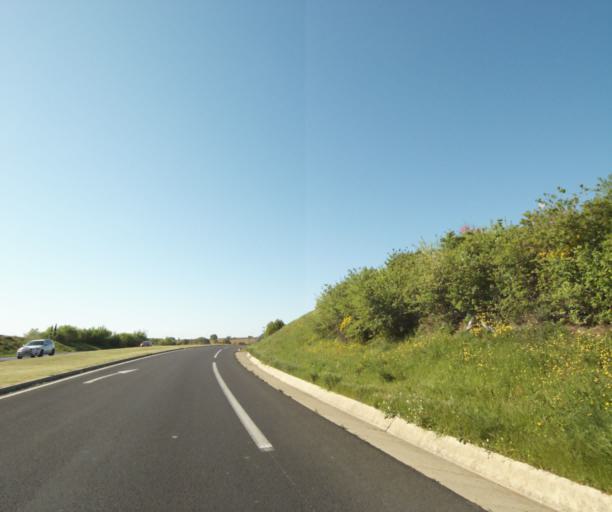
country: FR
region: Languedoc-Roussillon
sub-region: Departement de l'Herault
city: Le Cres
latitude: 43.6330
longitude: 3.9351
